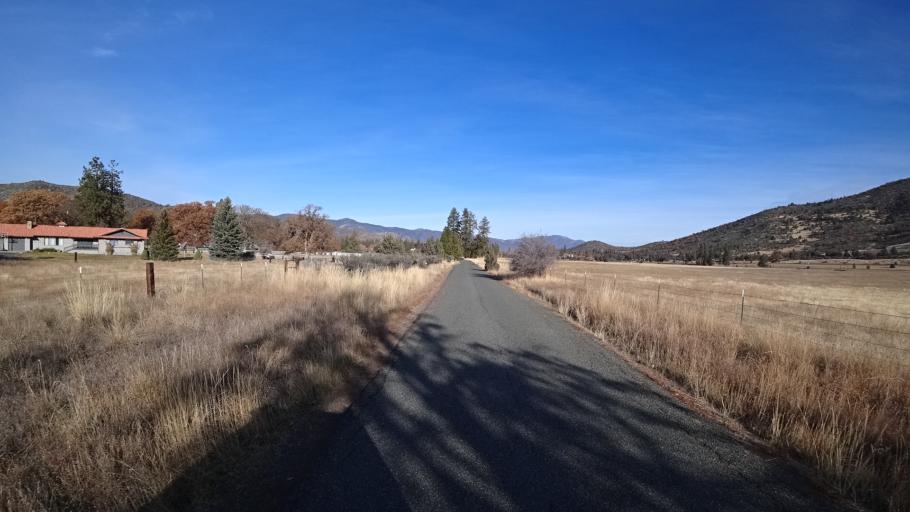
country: US
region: California
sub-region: Siskiyou County
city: Yreka
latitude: 41.6754
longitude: -122.6325
